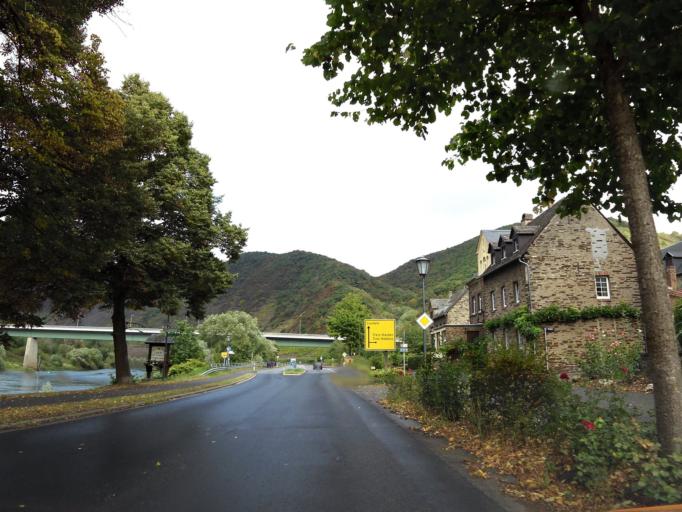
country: DE
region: Rheinland-Pfalz
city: Bruttig-Fankel
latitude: 50.1360
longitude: 7.2354
